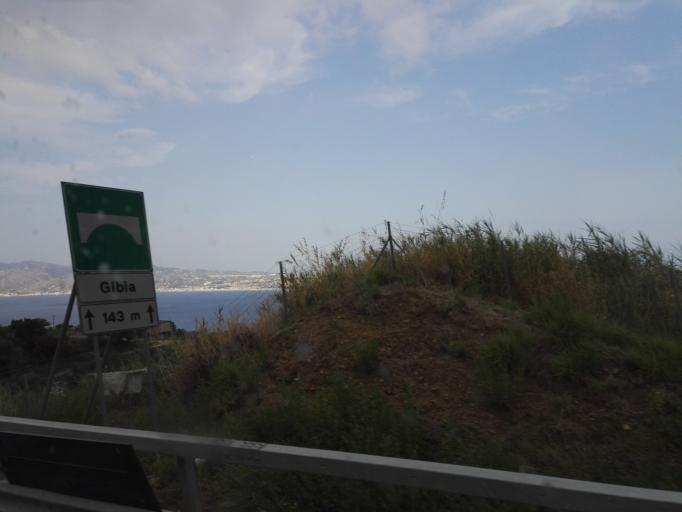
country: IT
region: Calabria
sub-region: Provincia di Reggio Calabria
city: Villa San Giovanni
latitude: 38.2365
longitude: 15.6765
